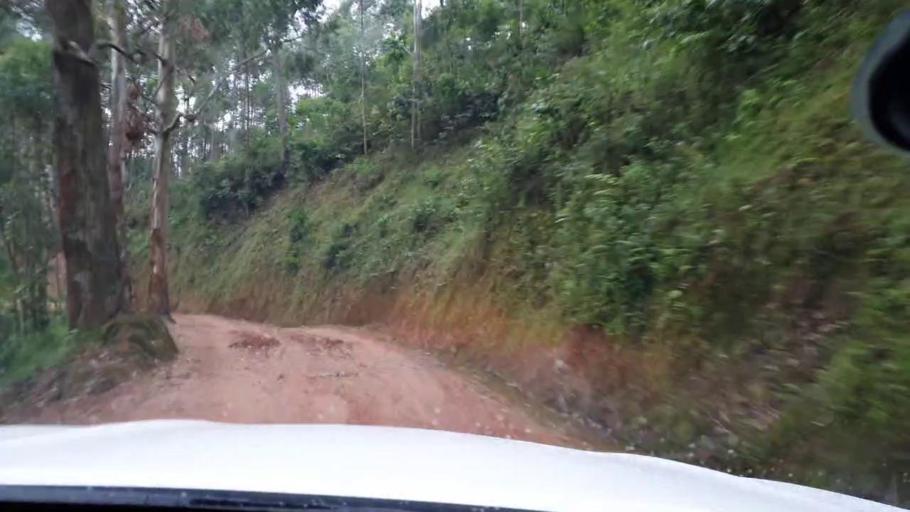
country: RW
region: Western Province
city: Cyangugu
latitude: -2.4129
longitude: 29.1961
